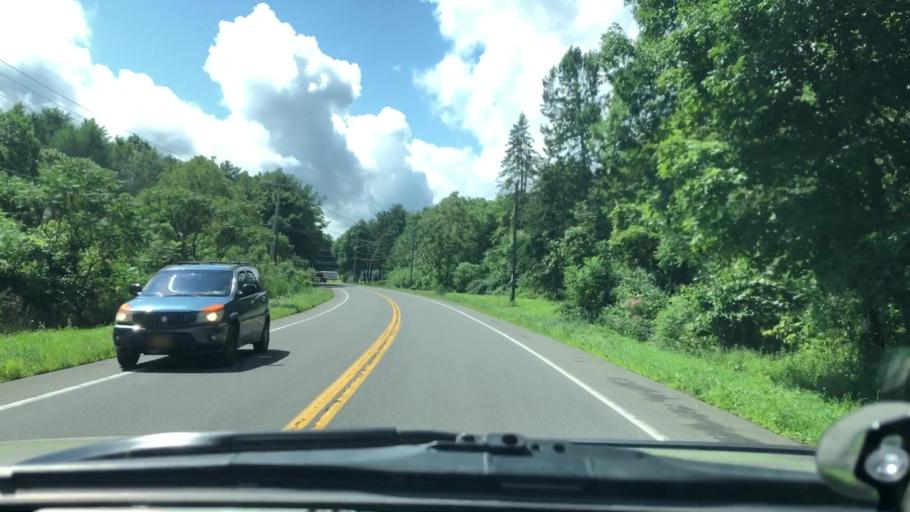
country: US
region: New York
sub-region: Greene County
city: Palenville
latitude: 42.2213
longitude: -73.9881
